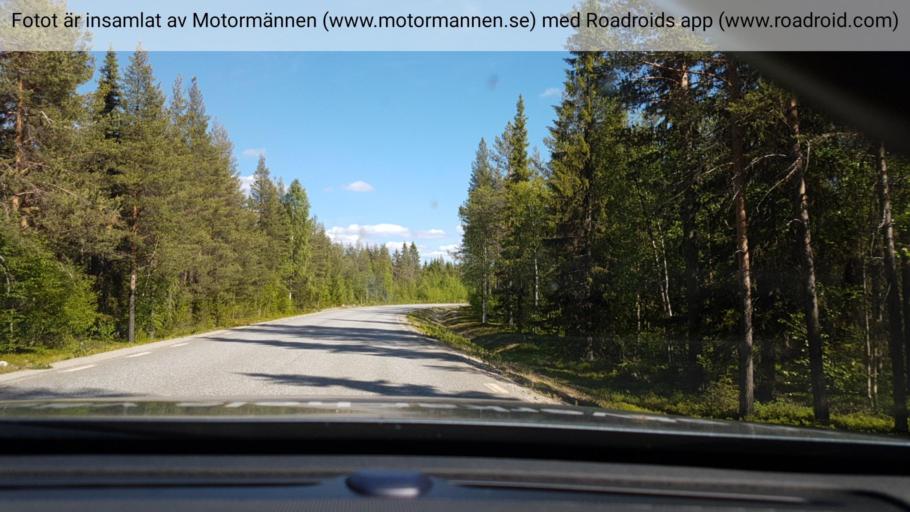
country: SE
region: Vaesterbotten
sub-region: Lycksele Kommun
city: Soderfors
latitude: 64.6209
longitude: 18.2943
